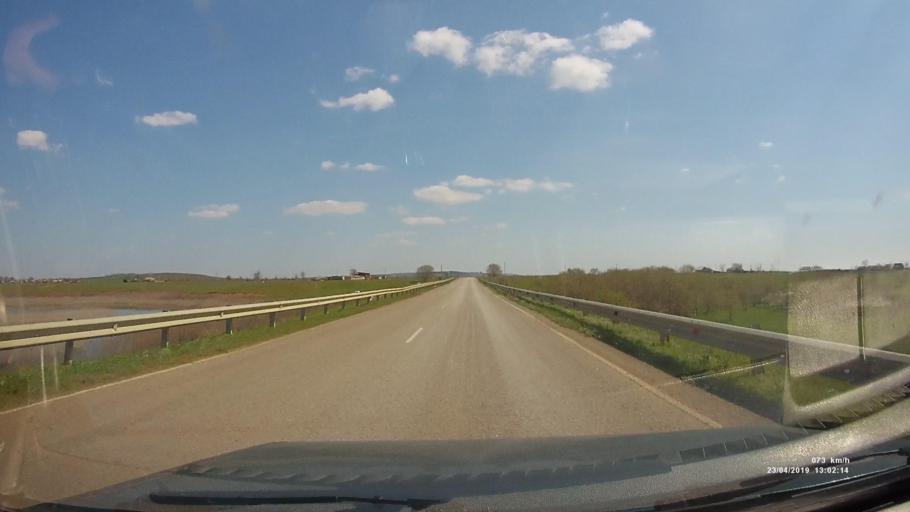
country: RU
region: Kalmykiya
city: Yashalta
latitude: 46.6014
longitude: 42.6663
